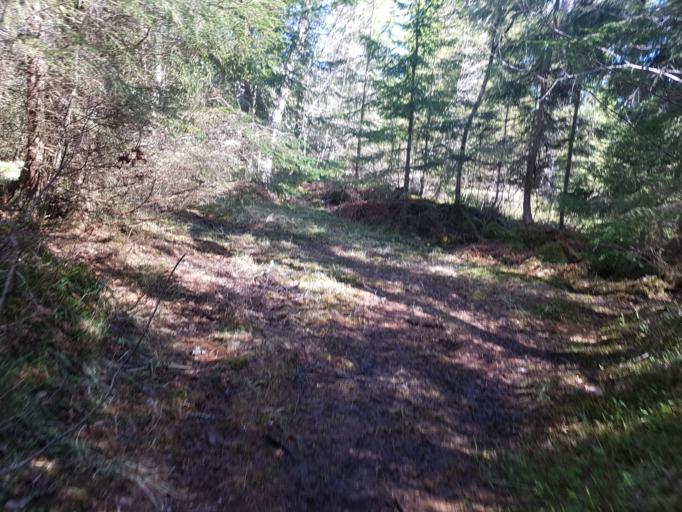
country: NO
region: Sor-Trondelag
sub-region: Trondheim
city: Trondheim
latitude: 63.4189
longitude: 10.3307
